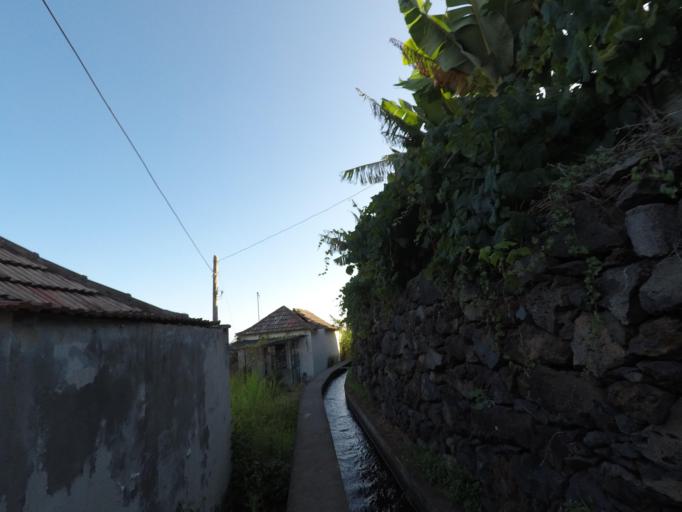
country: PT
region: Madeira
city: Camara de Lobos
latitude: 32.6465
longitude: -16.9473
